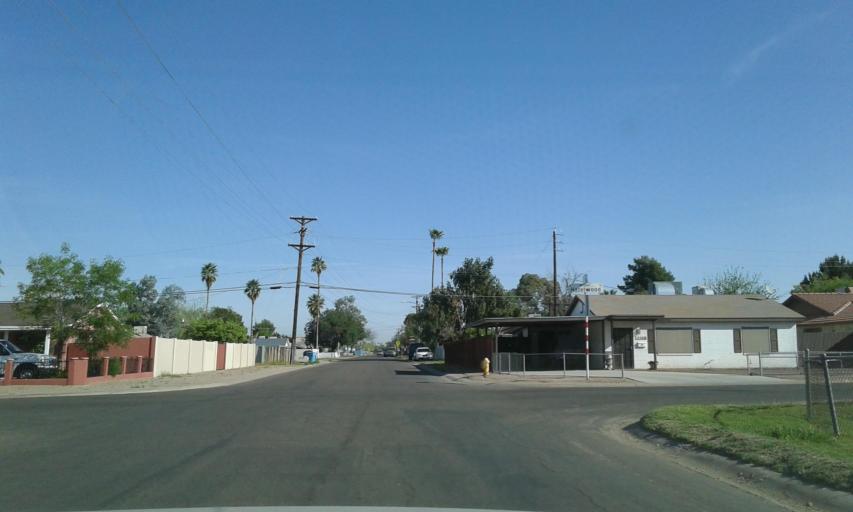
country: US
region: Arizona
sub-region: Maricopa County
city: Phoenix
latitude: 33.5039
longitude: -112.1062
